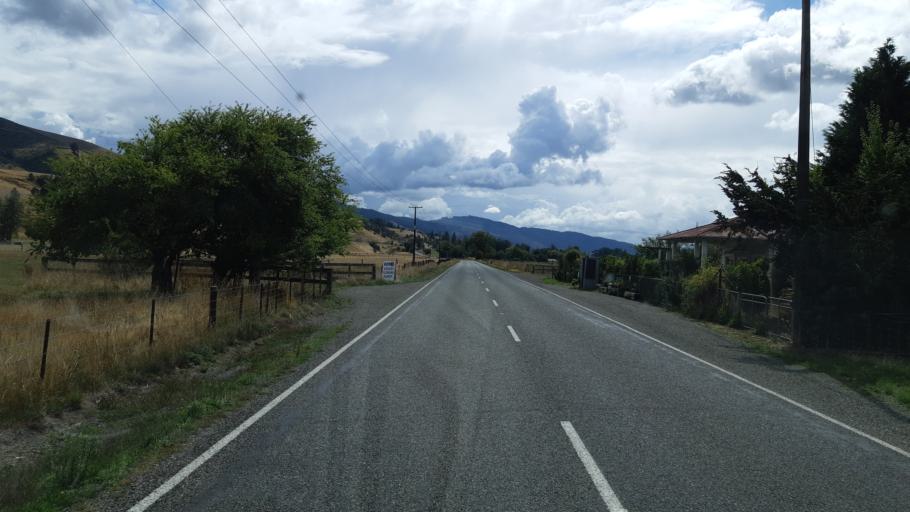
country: NZ
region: Tasman
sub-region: Tasman District
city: Wakefield
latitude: -41.5153
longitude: 172.7956
